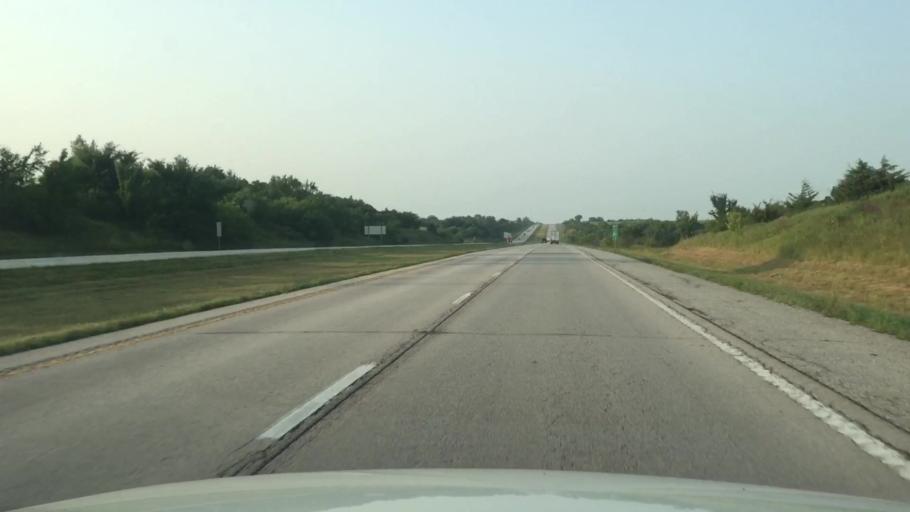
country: US
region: Iowa
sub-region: Decatur County
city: Lamoni
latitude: 40.4757
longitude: -93.9741
